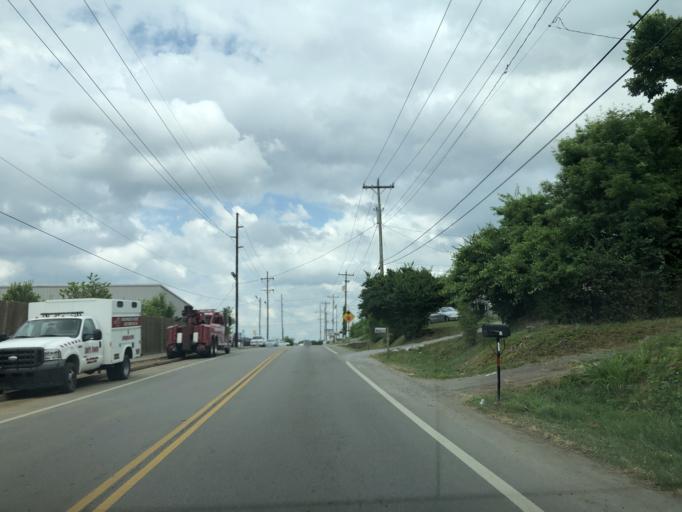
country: US
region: Tennessee
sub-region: Davidson County
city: Lakewood
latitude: 36.2625
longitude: -86.6829
